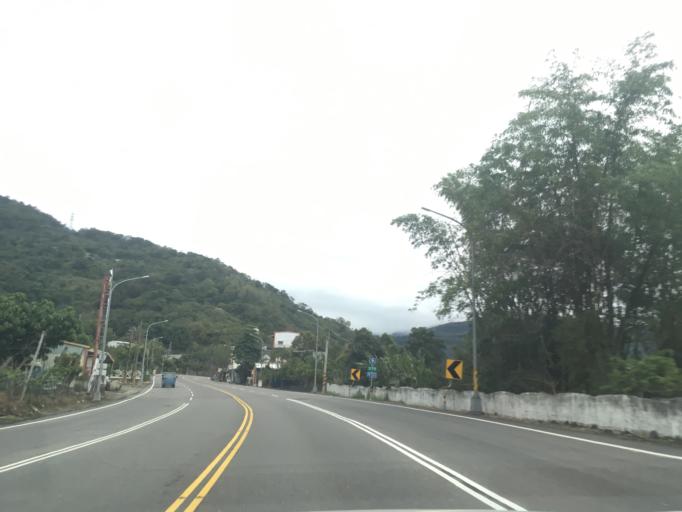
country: TW
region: Taiwan
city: Taitung City
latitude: 22.7476
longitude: 121.0565
